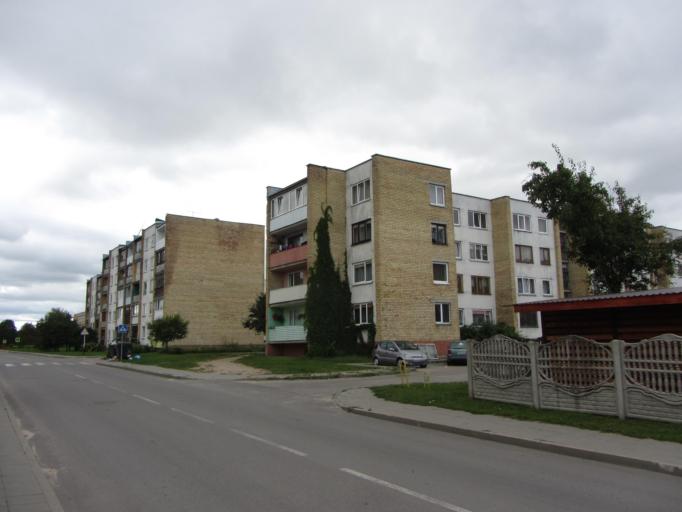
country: LT
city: Salcininkai
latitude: 54.3108
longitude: 25.3810
